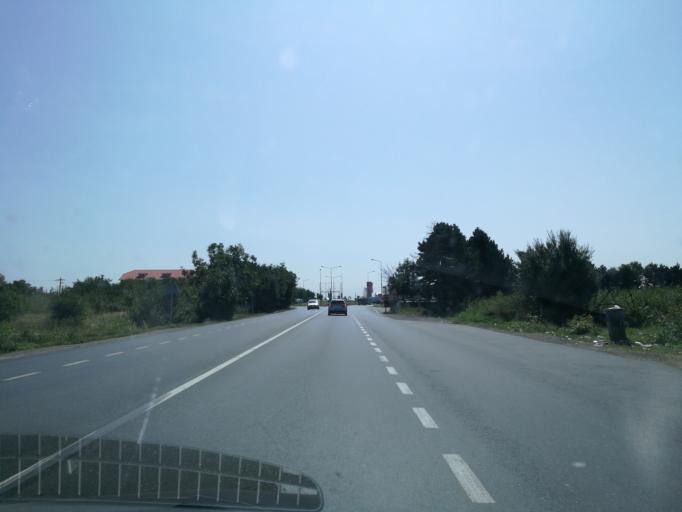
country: RO
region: Vrancea
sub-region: Comuna Tifesti
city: Igesti
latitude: 45.8469
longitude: 27.2104
